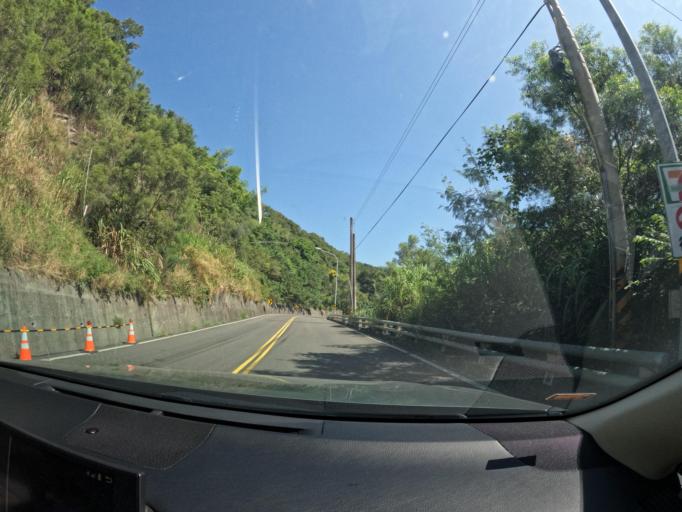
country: TW
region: Taiwan
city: Yujing
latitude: 23.1513
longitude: 120.7573
